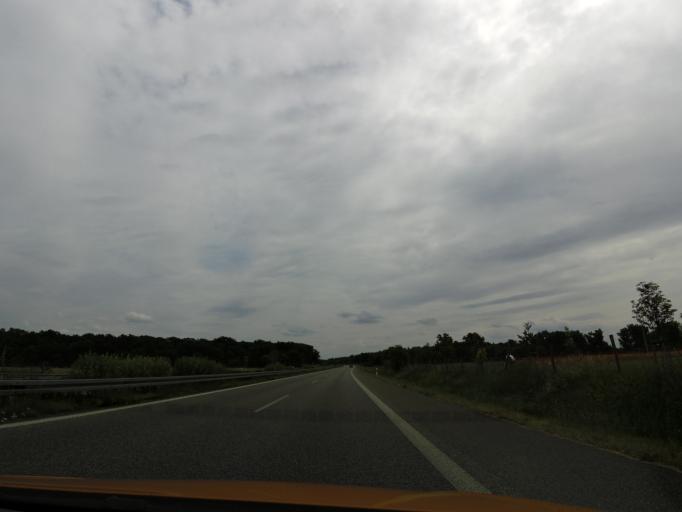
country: DE
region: Brandenburg
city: Grossbeeren
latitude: 52.3781
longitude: 13.3292
